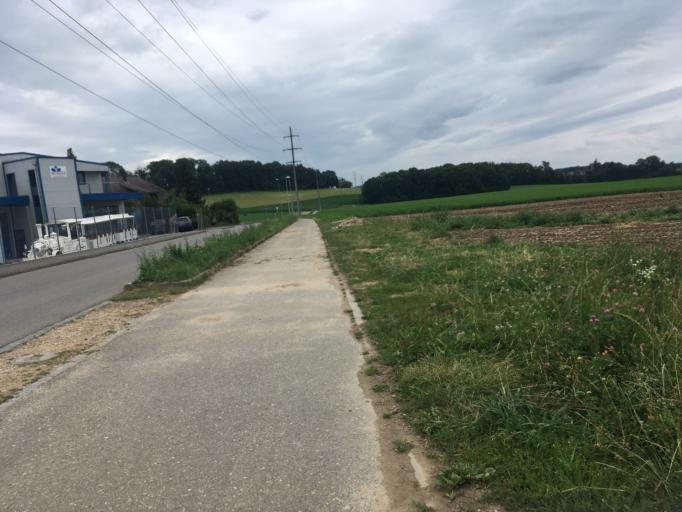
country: CH
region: Fribourg
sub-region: See District
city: Gurwolf
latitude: 46.9162
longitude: 7.1051
